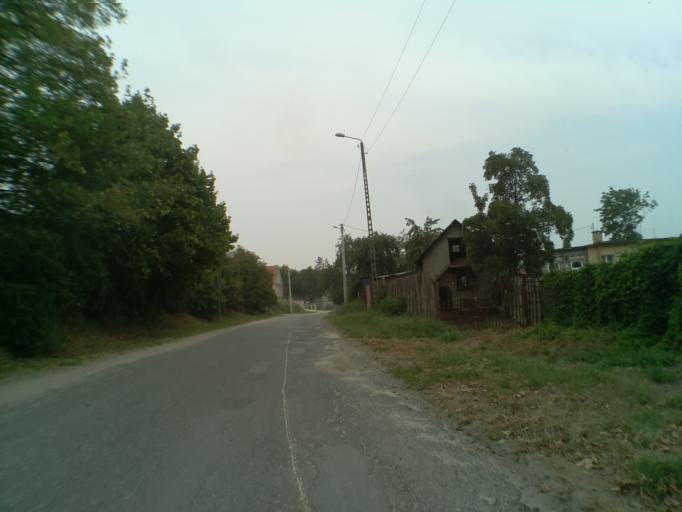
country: PL
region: Lower Silesian Voivodeship
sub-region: Powiat swidnicki
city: Strzegom
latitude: 50.9758
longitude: 16.3068
